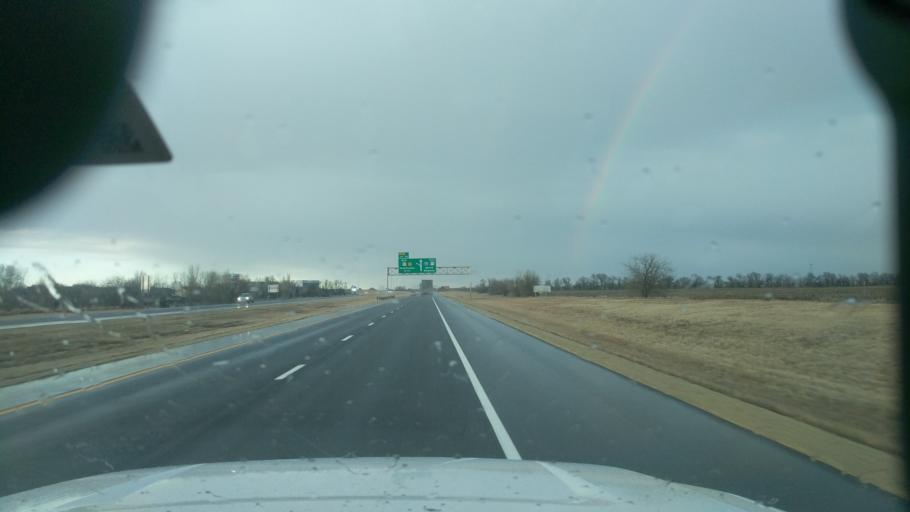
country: US
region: Kansas
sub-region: Harvey County
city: Newton
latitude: 38.0160
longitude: -97.3278
